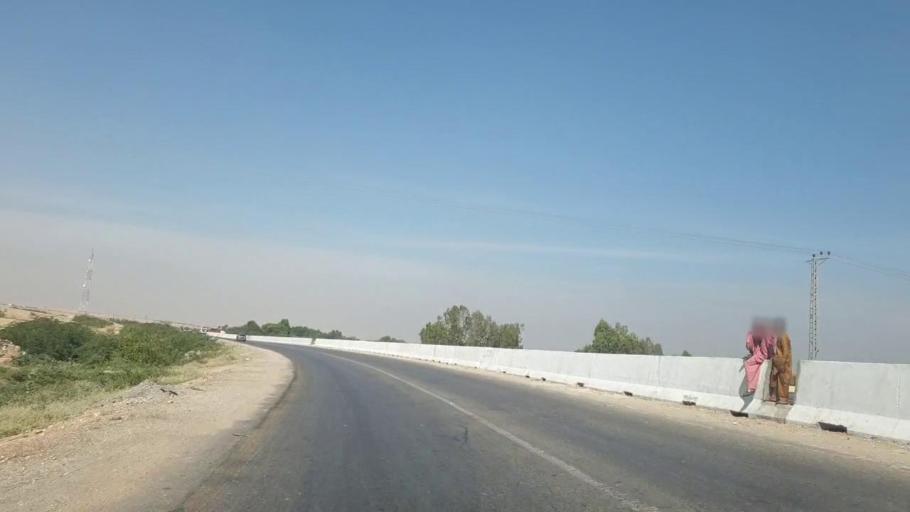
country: PK
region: Sindh
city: Hala
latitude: 25.7133
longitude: 68.2959
